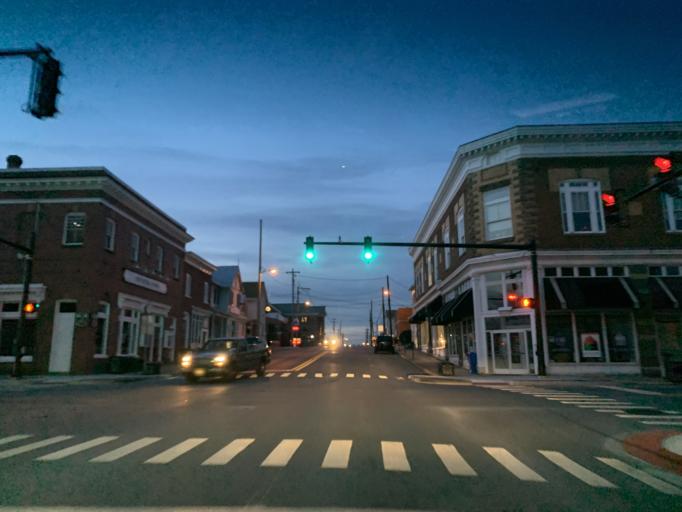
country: US
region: West Virginia
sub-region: Jefferson County
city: Charles Town
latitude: 39.2897
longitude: -77.8602
